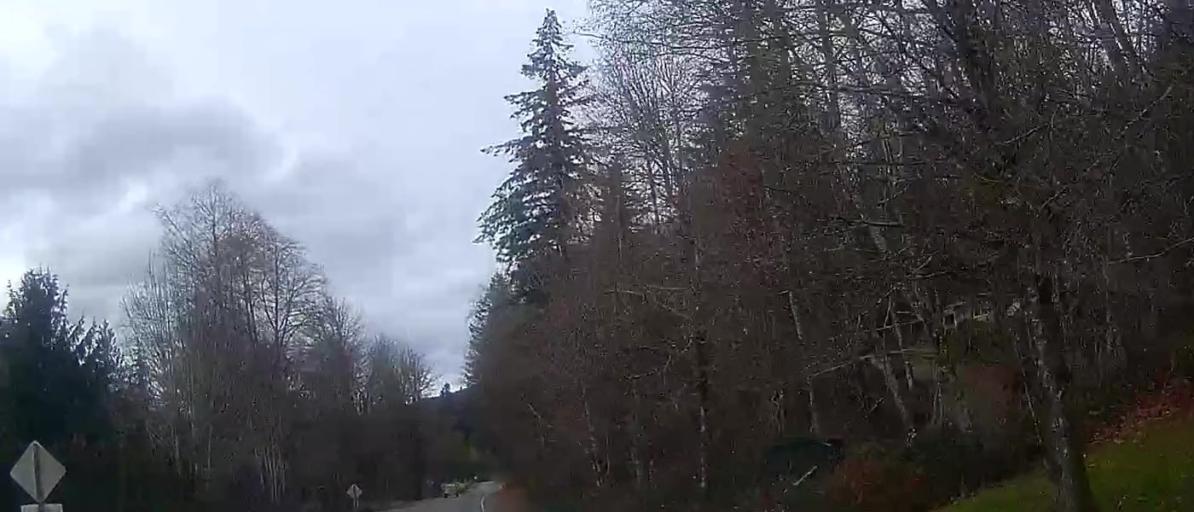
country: US
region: Washington
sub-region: Skagit County
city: Sedro-Woolley
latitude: 48.5803
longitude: -122.2522
